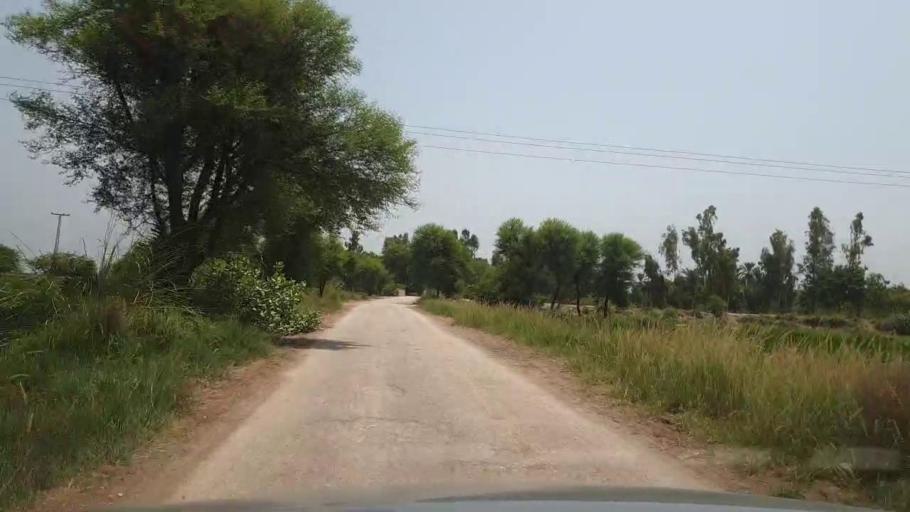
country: PK
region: Sindh
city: Ratodero
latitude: 27.7957
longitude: 68.3469
